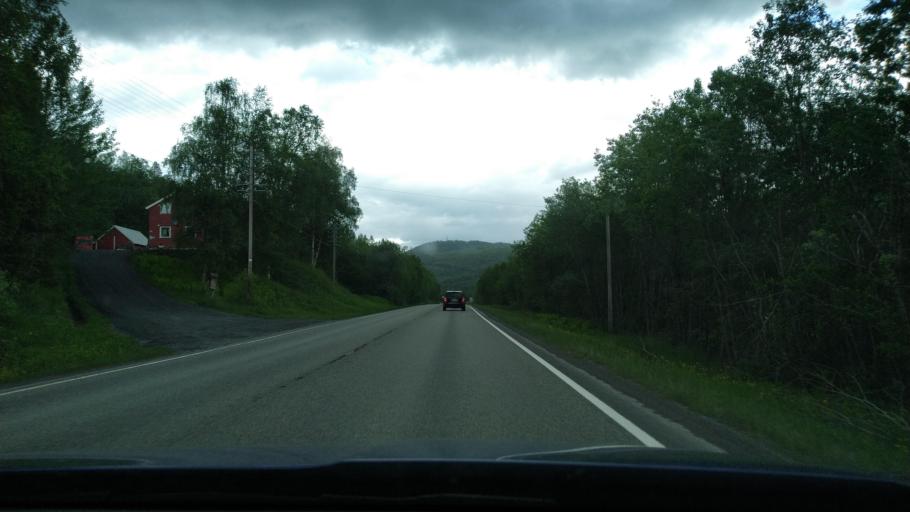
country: NO
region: Troms
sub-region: Malselv
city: Moen
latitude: 68.9792
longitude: 18.5053
